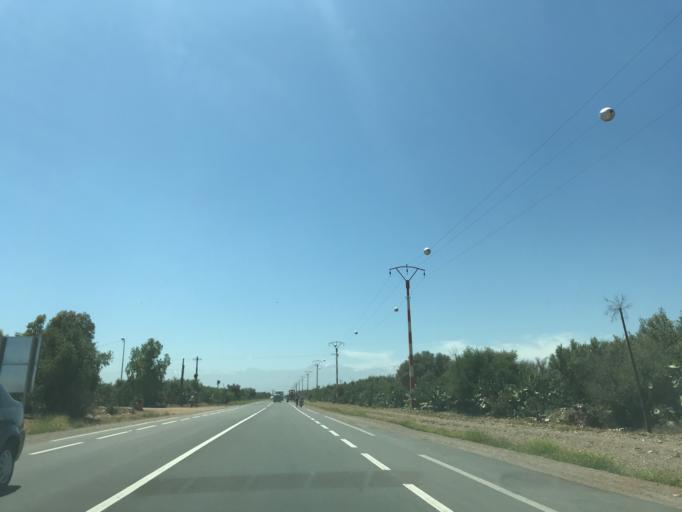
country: MA
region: Marrakech-Tensift-Al Haouz
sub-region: Marrakech
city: Marrakesh
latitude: 31.5437
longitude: -8.0023
